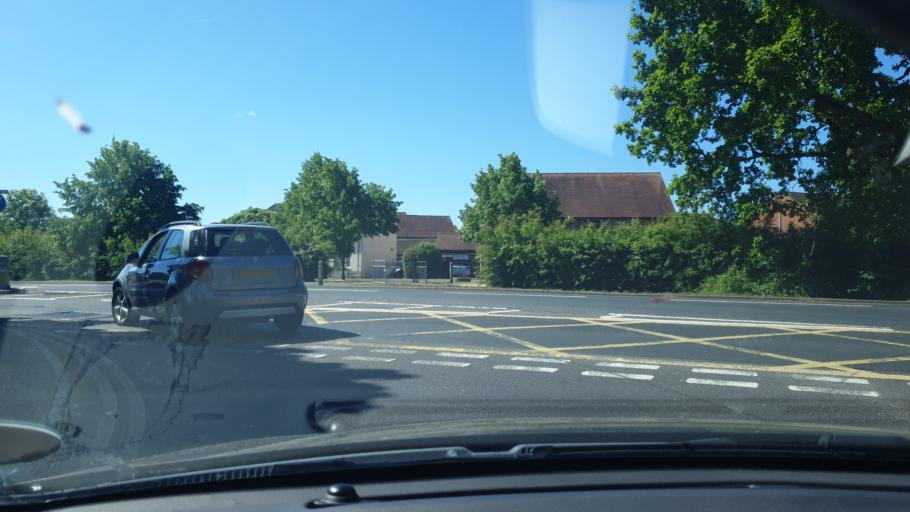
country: GB
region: England
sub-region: Essex
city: Colchester
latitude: 51.9149
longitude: 0.9262
